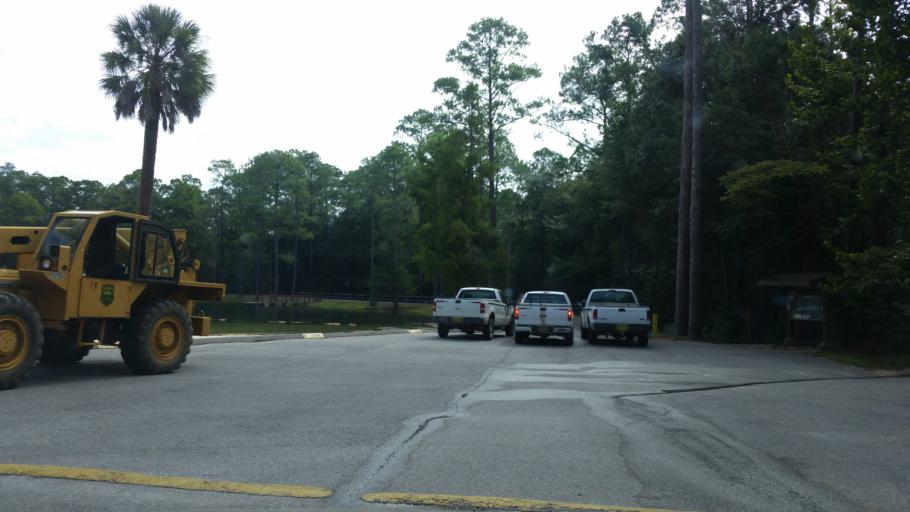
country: US
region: Florida
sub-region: Santa Rosa County
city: Point Baker
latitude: 30.8605
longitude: -86.8531
